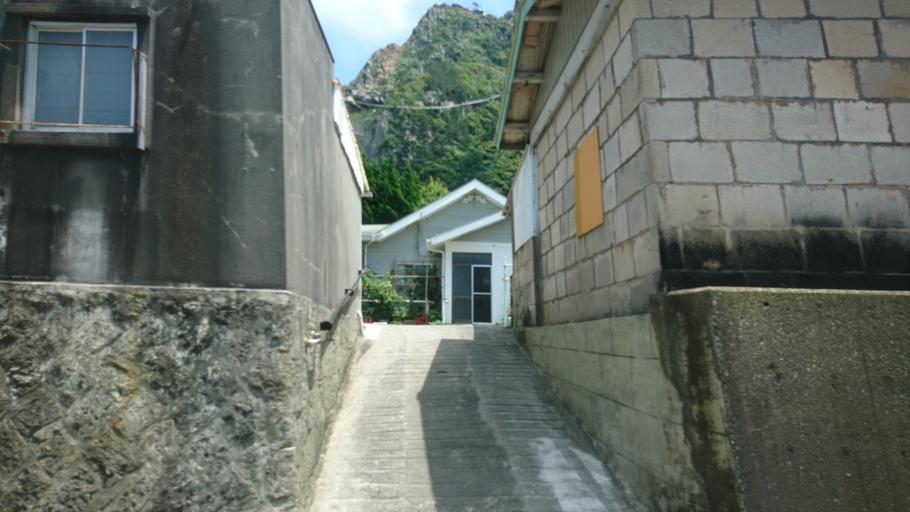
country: JP
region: Shizuoka
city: Shimoda
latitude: 34.4220
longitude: 139.2831
